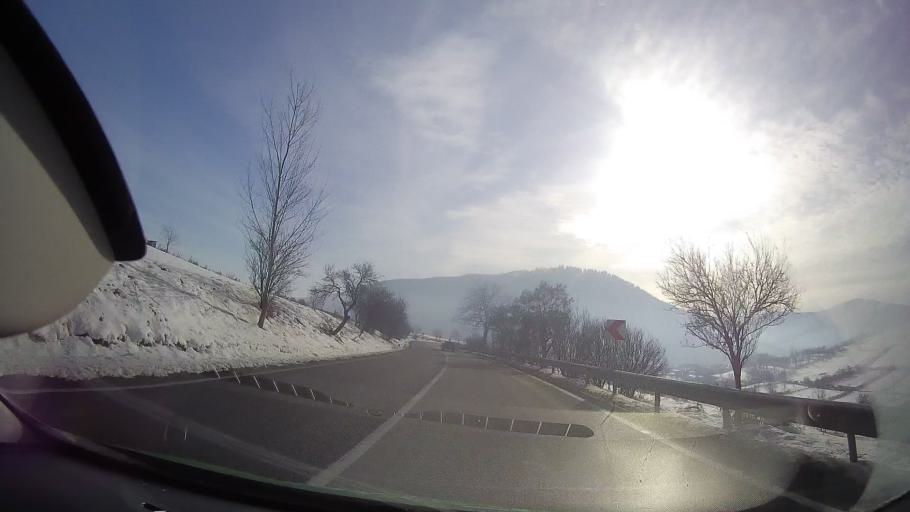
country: RO
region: Neamt
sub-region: Comuna Garcina
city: Garcina
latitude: 46.9812
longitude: 26.3582
